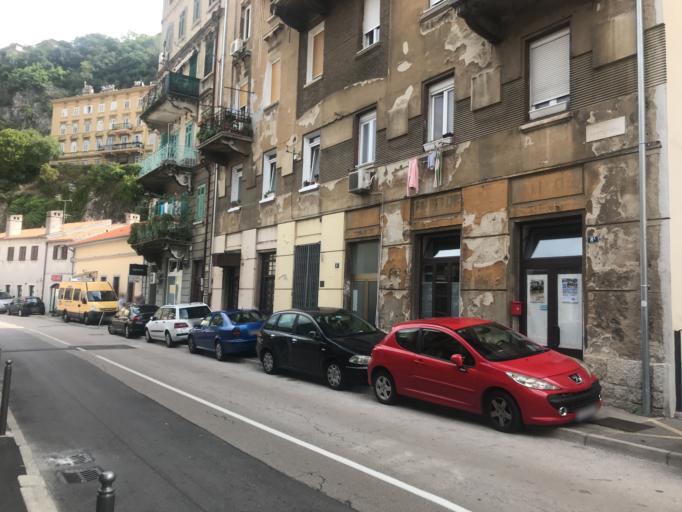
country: HR
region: Primorsko-Goranska
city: Drenova
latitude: 45.3294
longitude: 14.4513
